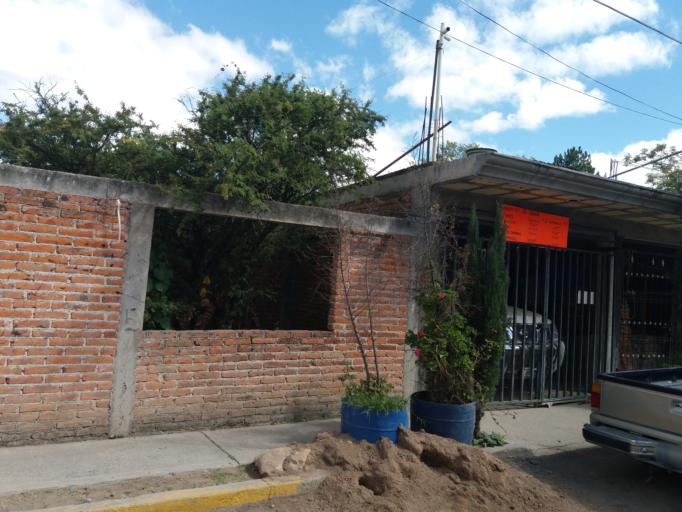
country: MX
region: Aguascalientes
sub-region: Aguascalientes
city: San Sebastian [Fraccionamiento]
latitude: 21.8014
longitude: -102.2747
